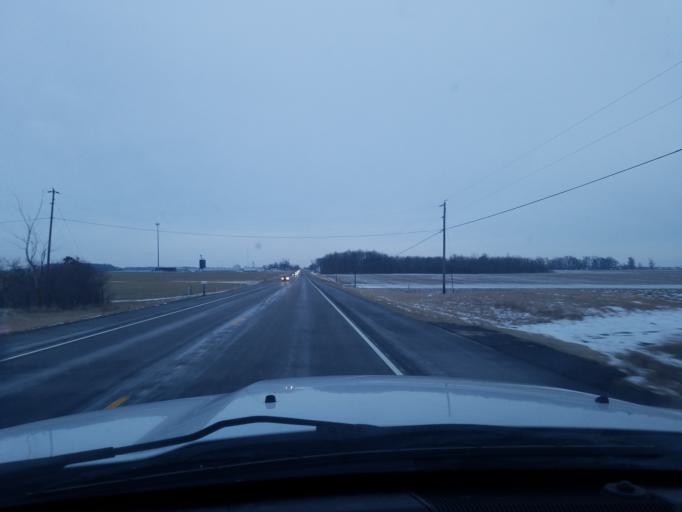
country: US
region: Indiana
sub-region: Randolph County
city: Parker City
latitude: 40.1932
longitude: -85.1952
